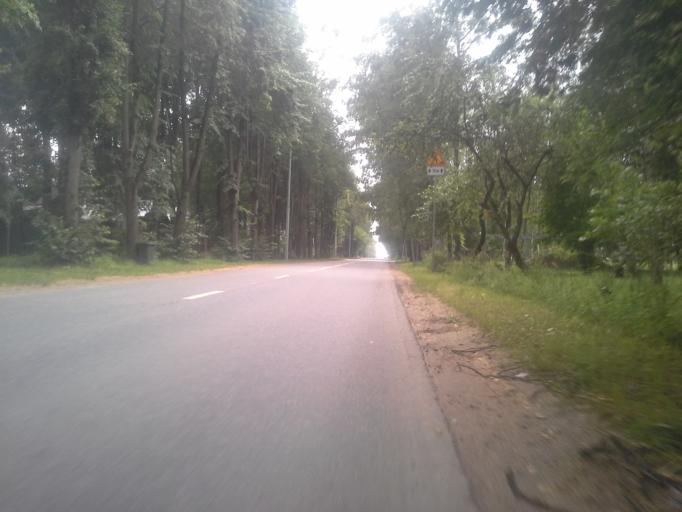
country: RU
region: Moskovskaya
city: Zvenigorod
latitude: 55.7246
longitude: 36.8313
